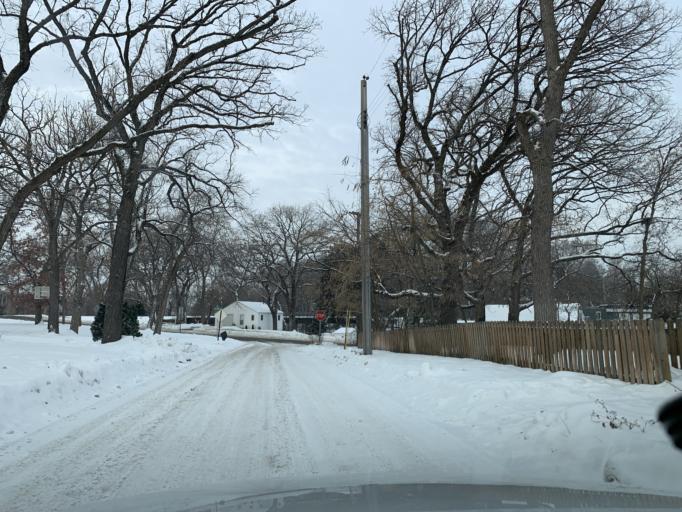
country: US
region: Minnesota
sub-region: Hennepin County
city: Saint Louis Park
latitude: 44.9210
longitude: -93.3525
